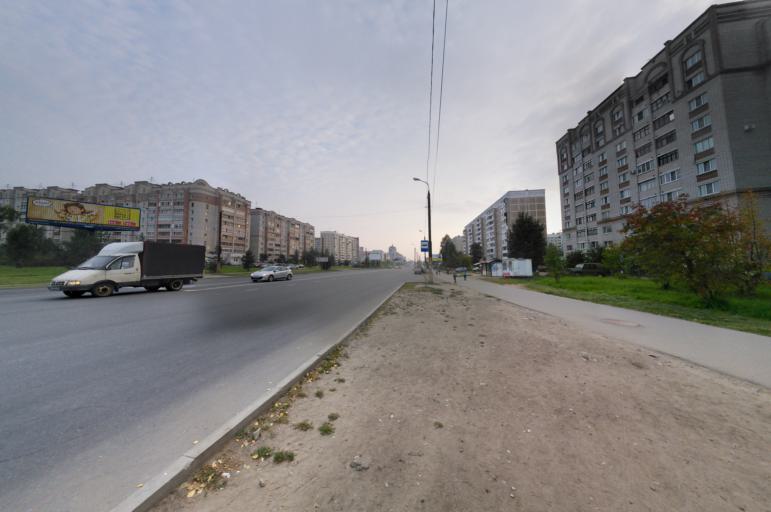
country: RU
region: Kostroma
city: Oktyabr'skiy
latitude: 57.7446
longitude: 41.0078
